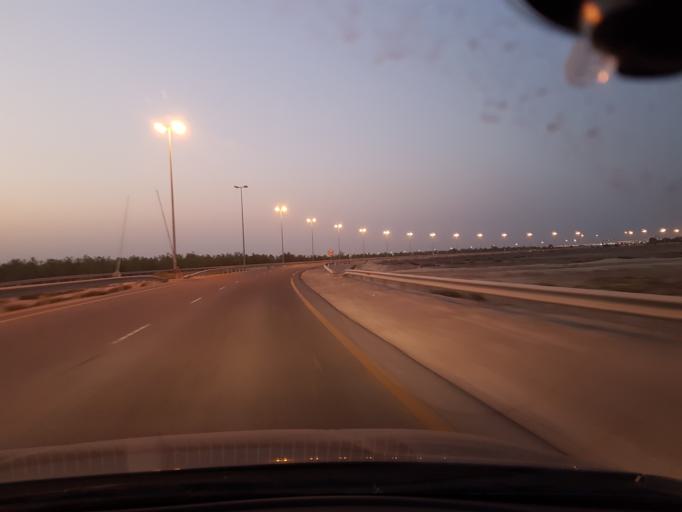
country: BH
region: Central Governorate
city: Dar Kulayb
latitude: 26.0102
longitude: 50.4840
